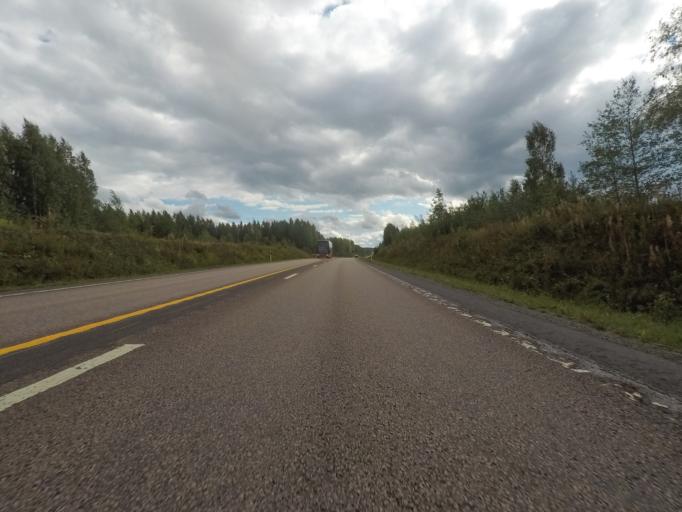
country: FI
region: Paijanne Tavastia
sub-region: Lahti
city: Hartola
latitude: 61.4115
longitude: 26.0410
